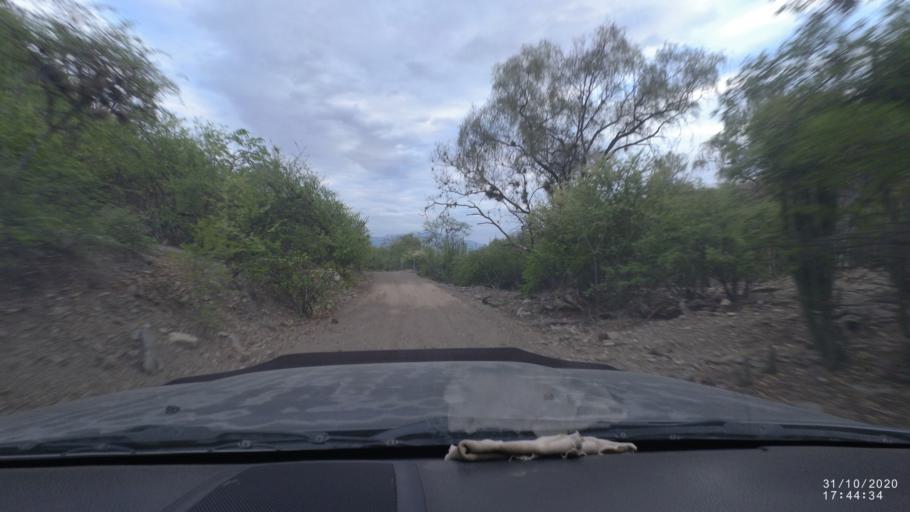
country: BO
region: Chuquisaca
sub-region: Provincia Zudanez
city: Mojocoya
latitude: -18.6111
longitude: -64.5468
